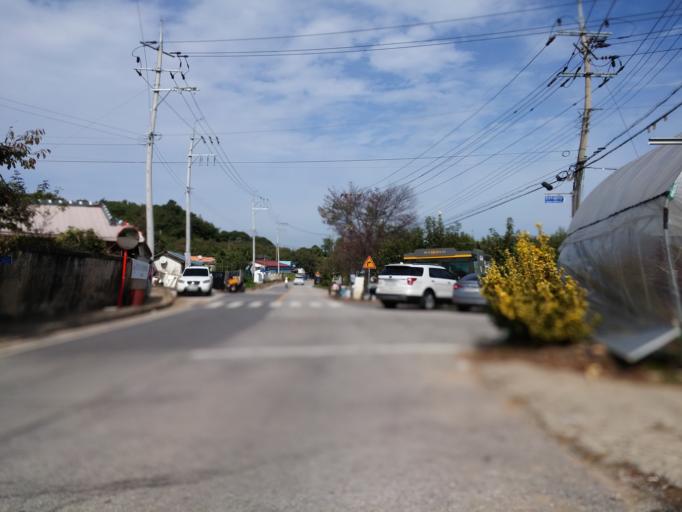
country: KR
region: Chungcheongnam-do
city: Yonmu
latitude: 36.1709
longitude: 127.1145
